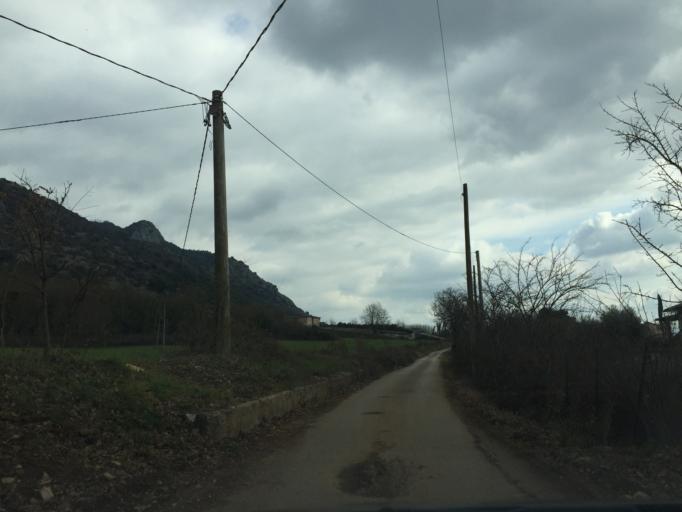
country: IT
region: Latium
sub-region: Provincia di Frosinone
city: Villa Santa Lucia
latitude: 41.4879
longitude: 13.7899
